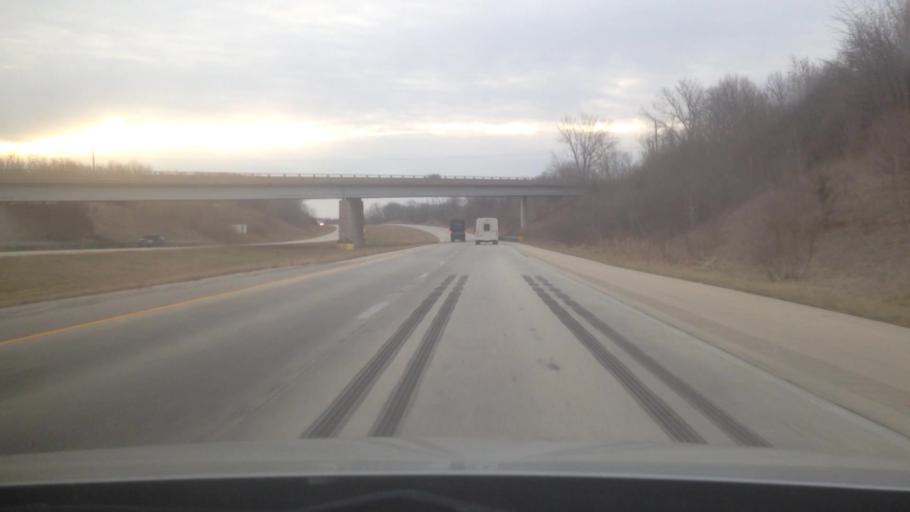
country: US
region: Illinois
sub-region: Macon County
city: Harristown
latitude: 39.8152
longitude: -89.0299
